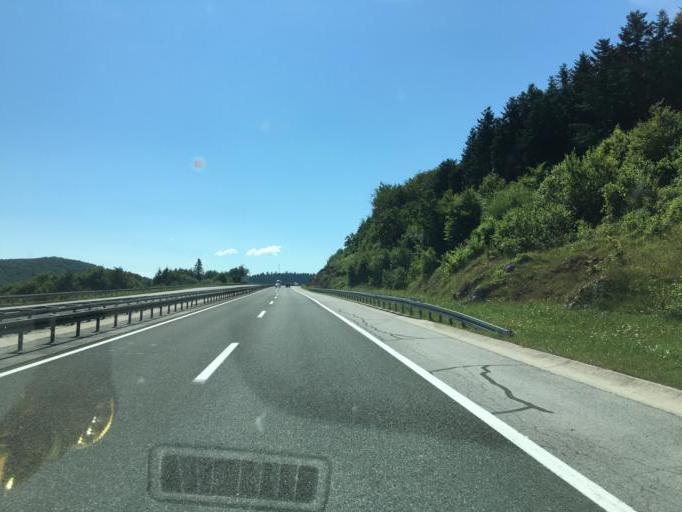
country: HR
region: Licko-Senjska
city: Otocac
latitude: 44.8588
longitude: 15.2159
